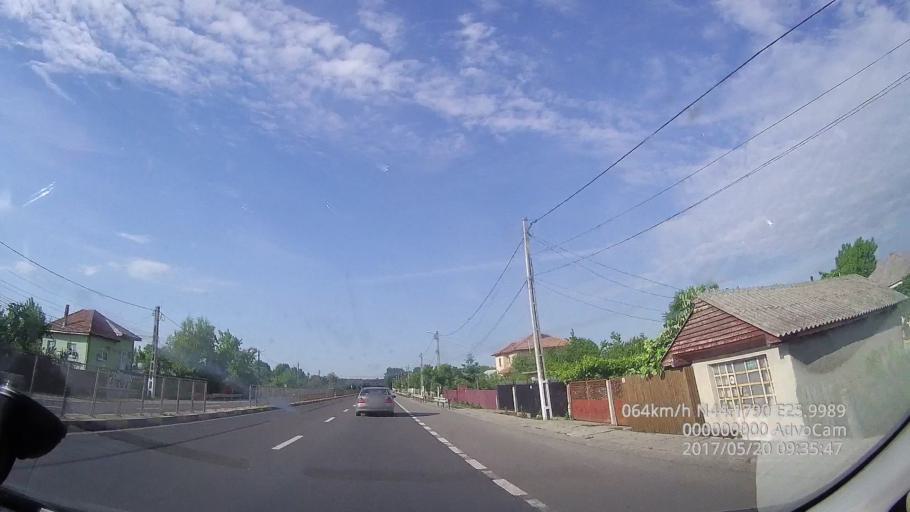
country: RO
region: Giurgiu
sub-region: Comuna Calugareni
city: Calugareni
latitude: 44.1789
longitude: 25.9988
